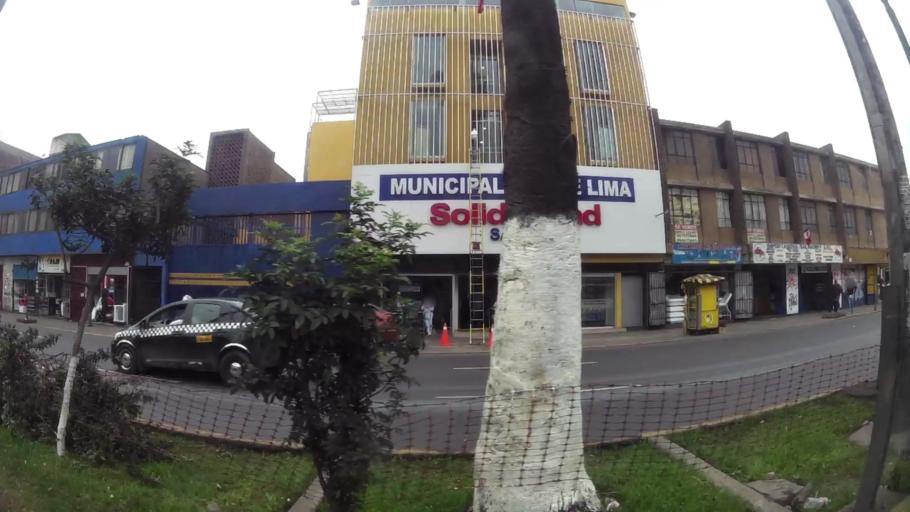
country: PE
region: Lima
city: Lima
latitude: -12.0609
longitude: -77.0297
